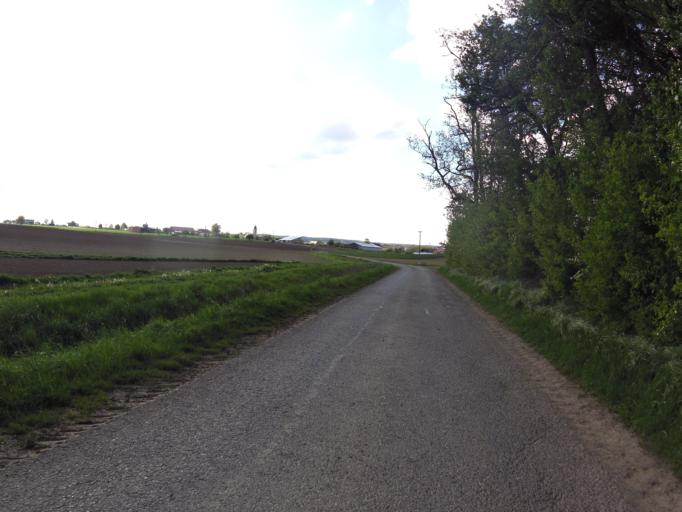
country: DE
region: Bavaria
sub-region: Regierungsbezirk Unterfranken
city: Unterpleichfeld
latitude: 49.8636
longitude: 10.0577
